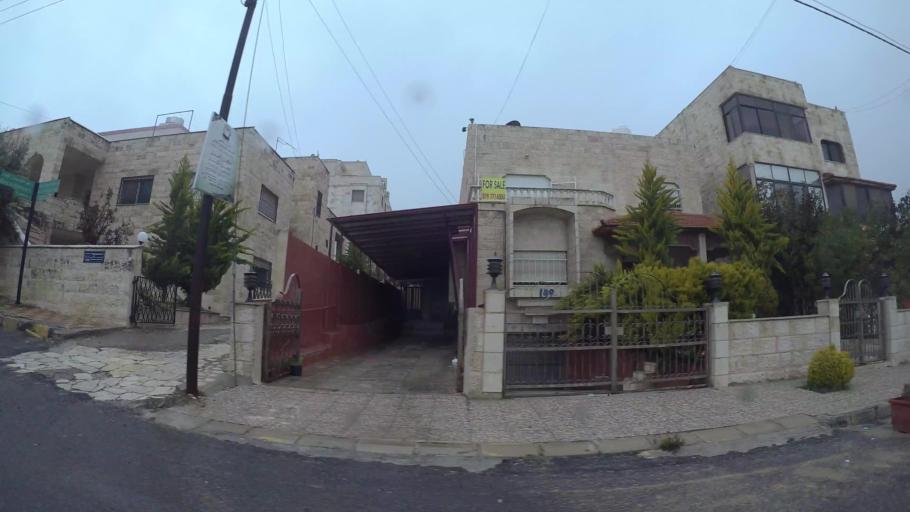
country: JO
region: Amman
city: Al Jubayhah
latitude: 32.0151
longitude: 35.8377
